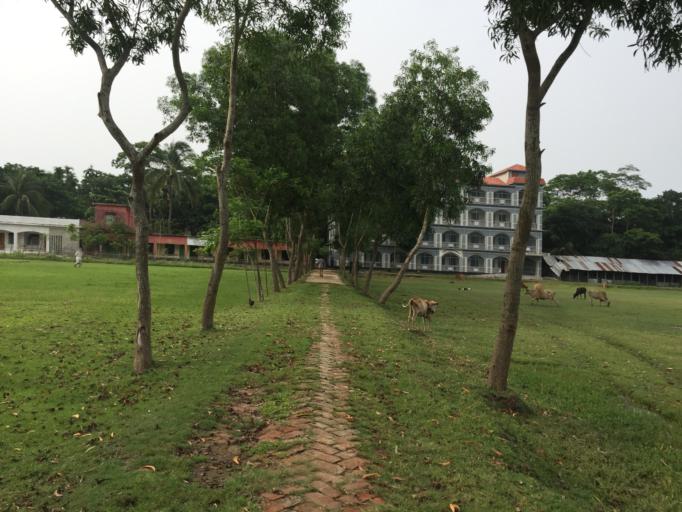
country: BD
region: Barisal
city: Mathba
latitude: 22.1895
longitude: 89.9257
